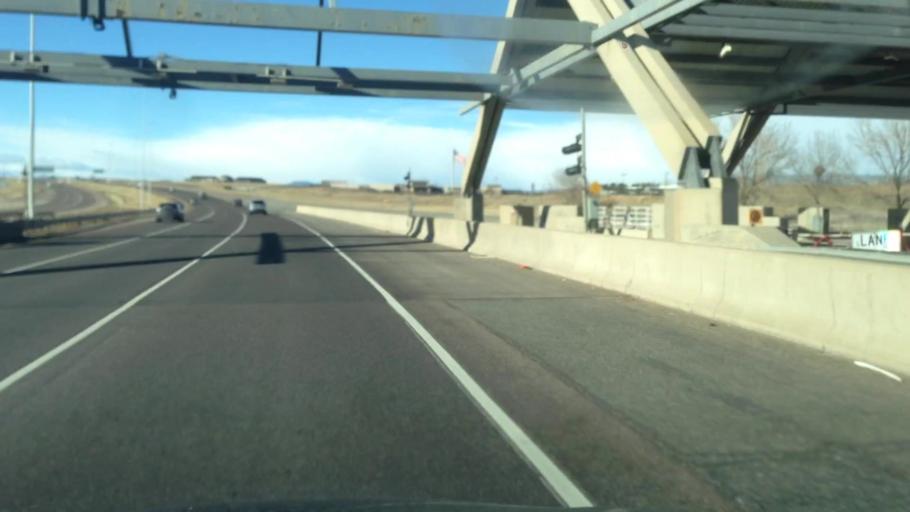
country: US
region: Colorado
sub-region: Arapahoe County
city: Dove Valley
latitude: 39.5565
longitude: -104.8220
